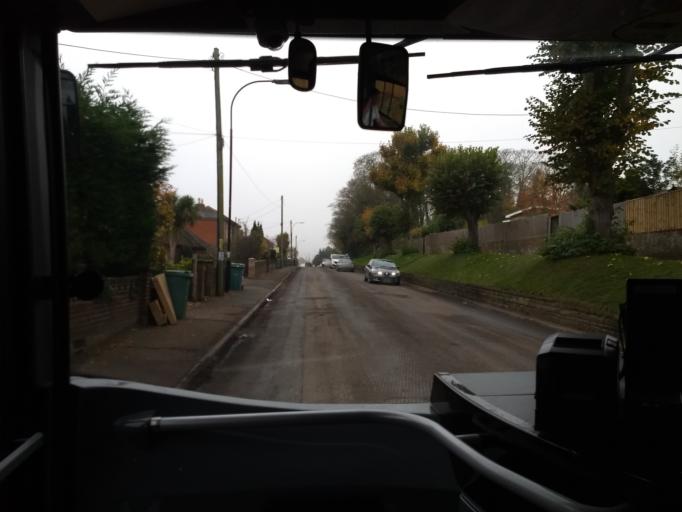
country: GB
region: England
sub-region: Isle of Wight
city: Brading
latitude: 50.6717
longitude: -1.1466
